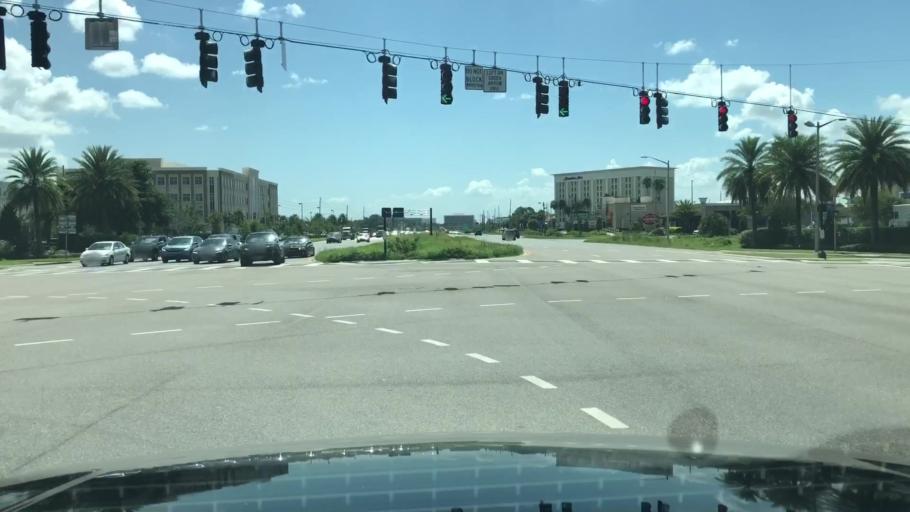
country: US
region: Florida
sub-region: Orange County
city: Tangelo Park
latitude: 28.4626
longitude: -81.4587
